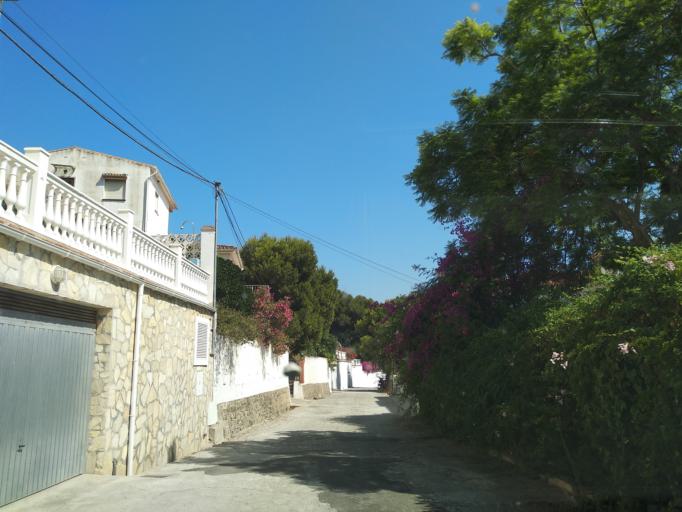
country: ES
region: Andalusia
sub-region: Provincia de Malaga
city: Valdes
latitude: 36.7173
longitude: -4.2020
